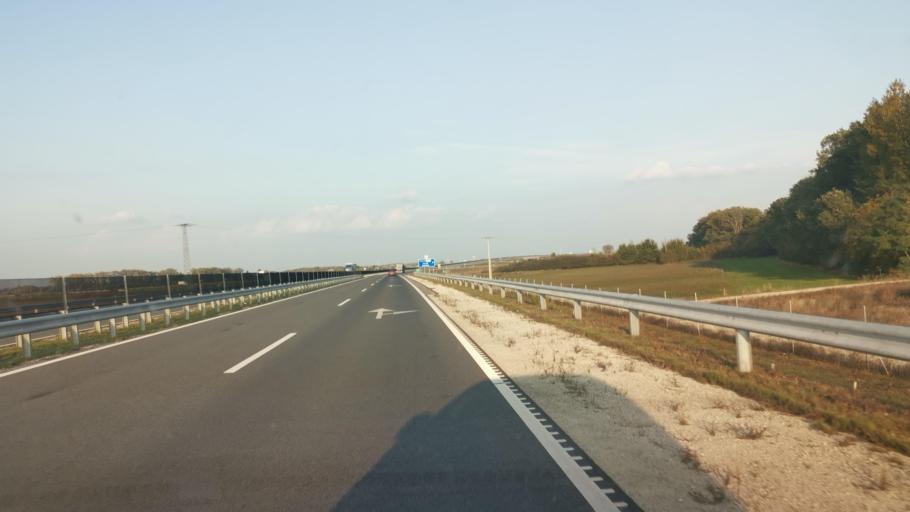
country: HU
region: Gyor-Moson-Sopron
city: Farad
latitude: 47.5875
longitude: 17.1842
